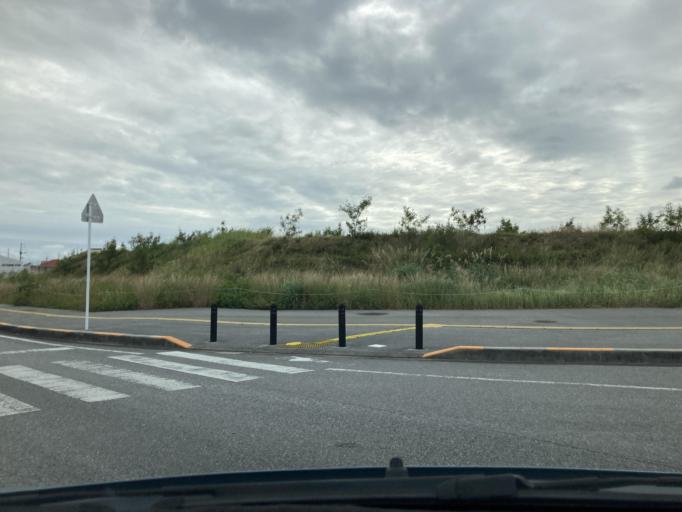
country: JP
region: Okinawa
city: Itoman
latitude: 26.1577
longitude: 127.6650
